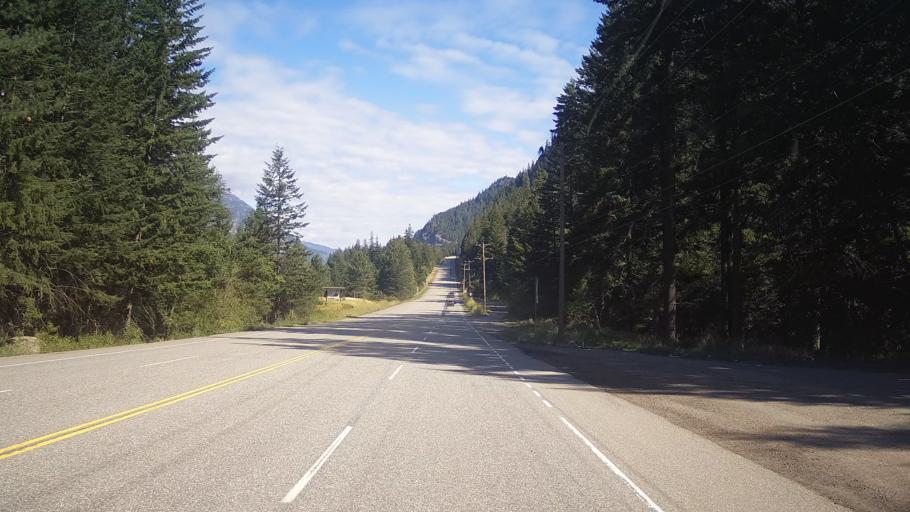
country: CA
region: British Columbia
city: Hope
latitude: 50.0520
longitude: -121.5415
